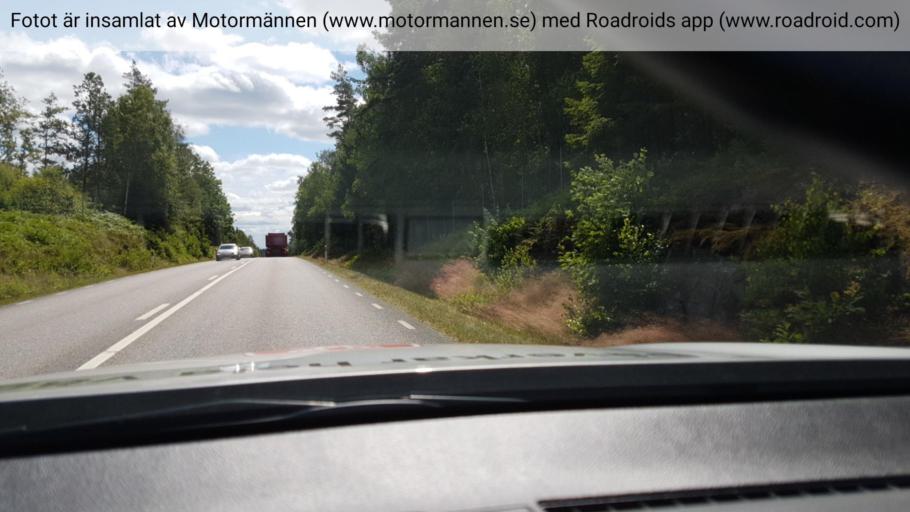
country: SE
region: Vaestra Goetaland
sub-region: Harryda Kommun
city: Ravlanda
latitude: 57.5649
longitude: 12.5129
